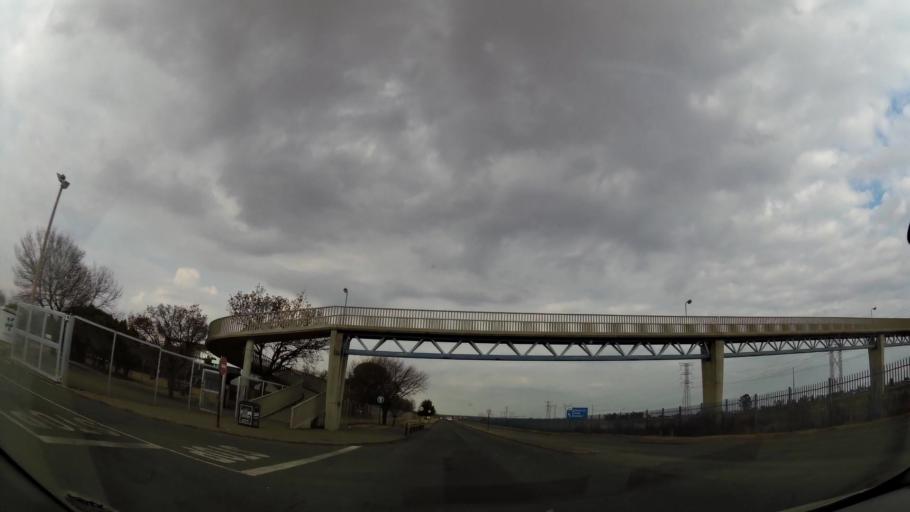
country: ZA
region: Orange Free State
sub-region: Fezile Dabi District Municipality
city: Sasolburg
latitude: -26.8337
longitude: 27.8643
